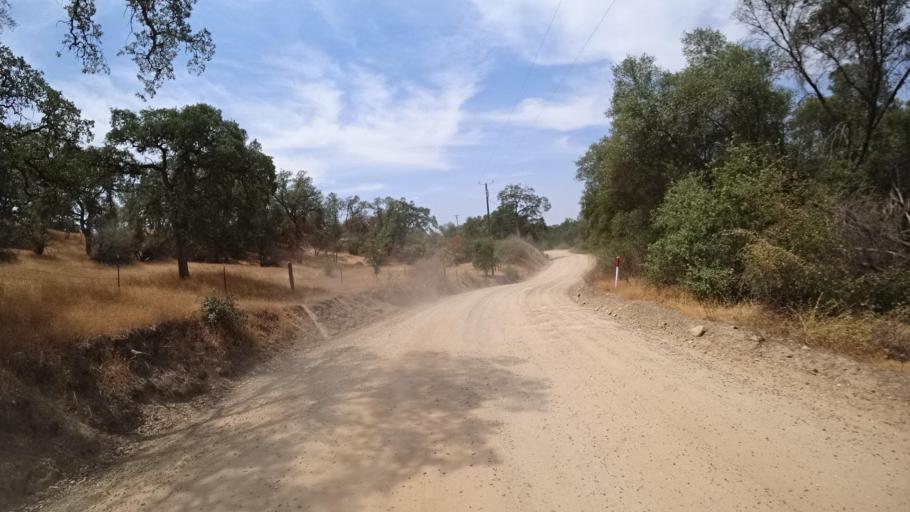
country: US
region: California
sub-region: Madera County
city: Ahwahnee
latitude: 37.4095
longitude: -119.8222
